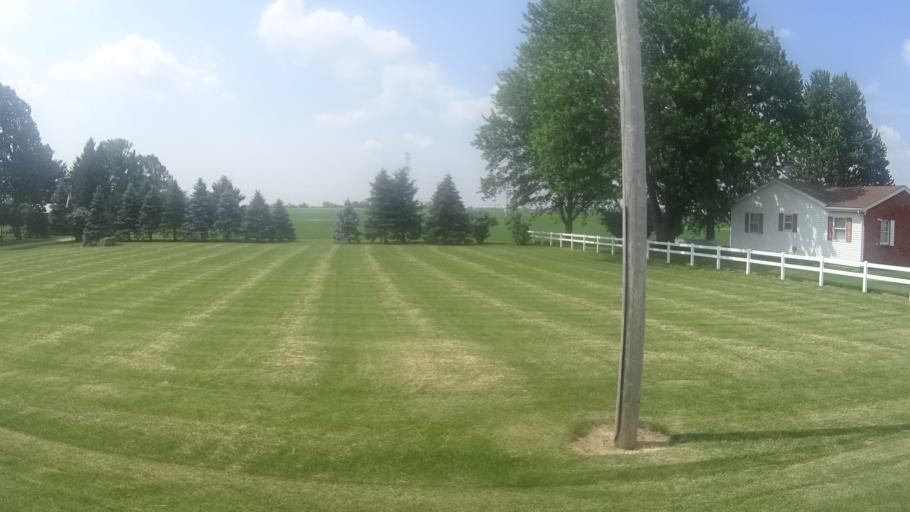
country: US
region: Ohio
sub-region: Erie County
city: Sandusky
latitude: 41.3528
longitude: -82.7059
